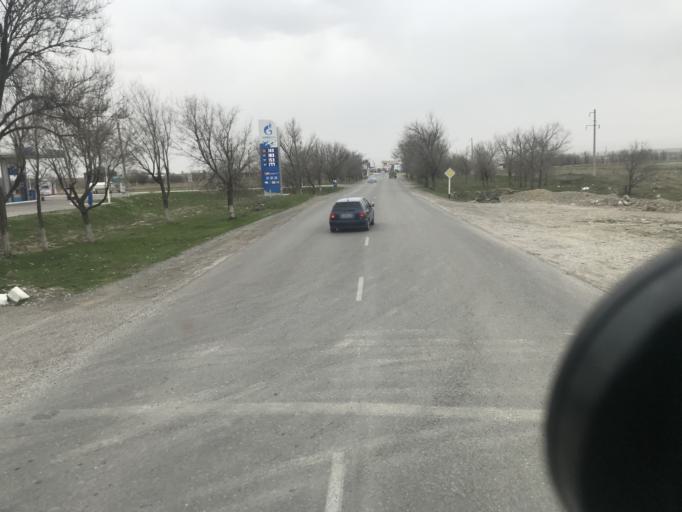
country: KZ
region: Ongtustik Qazaqstan
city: Aksu
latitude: 42.4775
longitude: 69.8138
